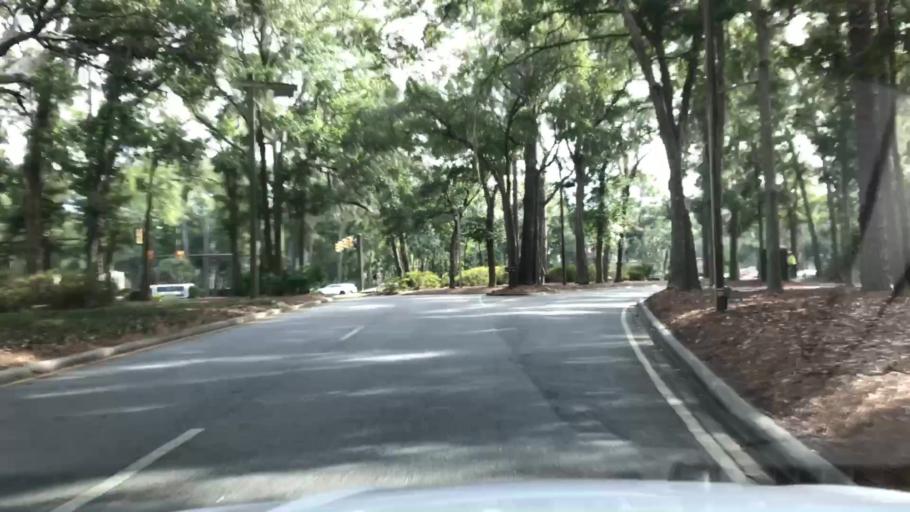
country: US
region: South Carolina
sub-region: Beaufort County
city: Hilton Head Island
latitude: 32.2156
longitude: -80.7215
